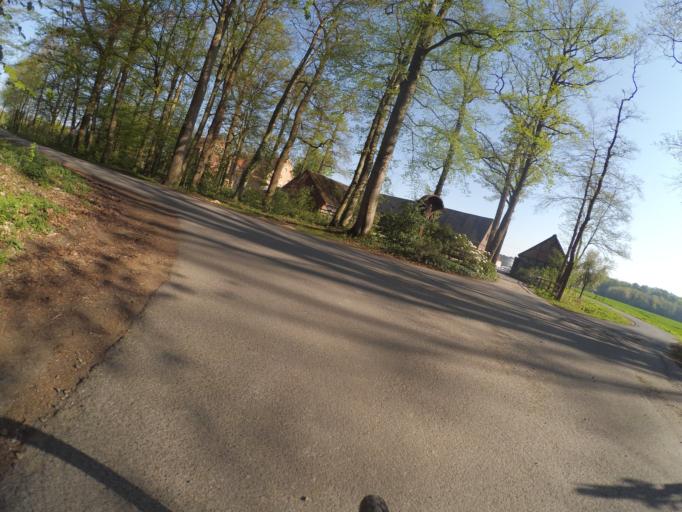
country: DE
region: North Rhine-Westphalia
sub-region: Regierungsbezirk Munster
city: Senden
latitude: 51.8551
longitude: 7.5155
